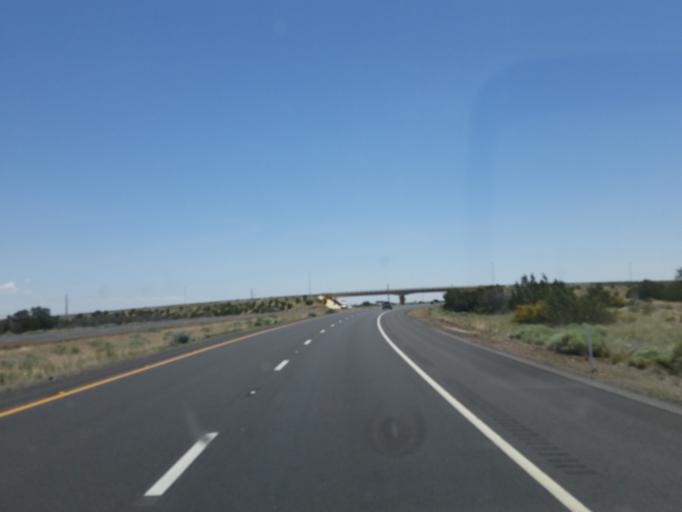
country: US
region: Arizona
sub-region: Coconino County
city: Flagstaff
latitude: 35.1618
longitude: -111.2757
